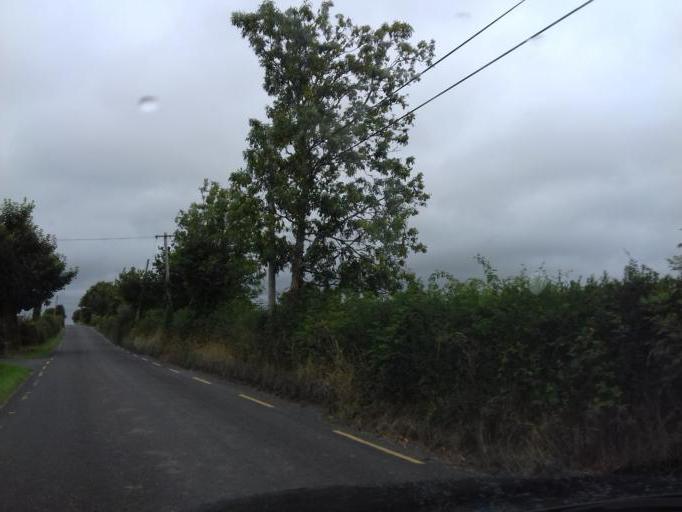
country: IE
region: Leinster
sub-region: County Carlow
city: Bagenalstown
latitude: 52.6172
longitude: -7.0360
